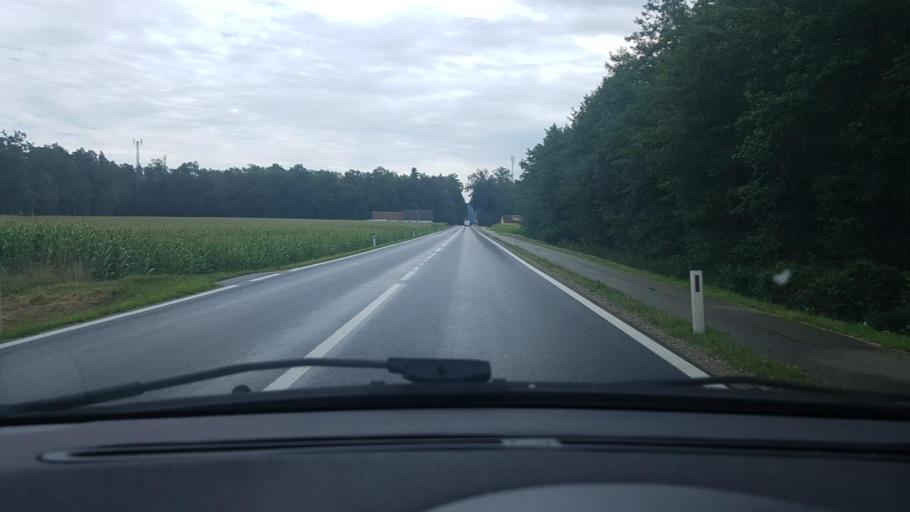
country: AT
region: Styria
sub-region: Politischer Bezirk Leibnitz
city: Strass in Steiermark
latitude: 46.7563
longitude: 15.6507
